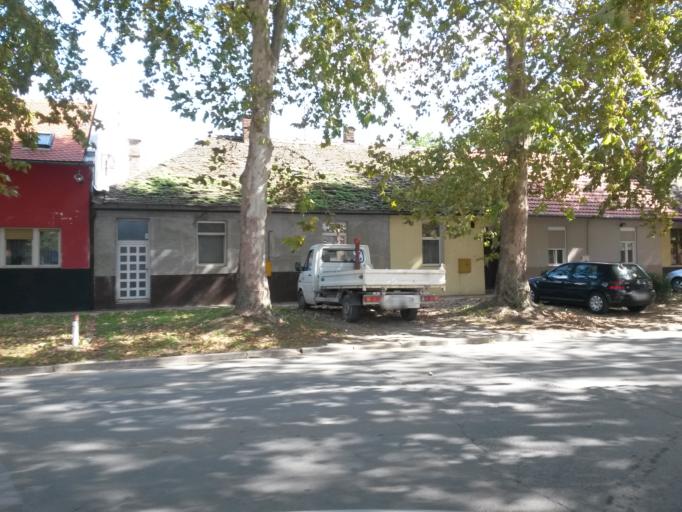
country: HR
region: Osjecko-Baranjska
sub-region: Grad Osijek
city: Osijek
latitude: 45.5554
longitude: 18.6721
